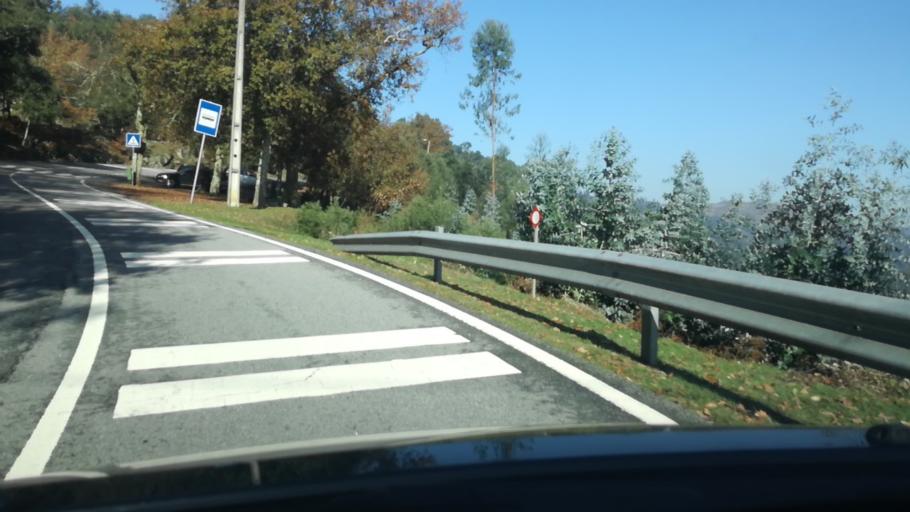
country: PT
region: Braga
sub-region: Guimaraes
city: Ponte
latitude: 41.5268
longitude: -8.3139
